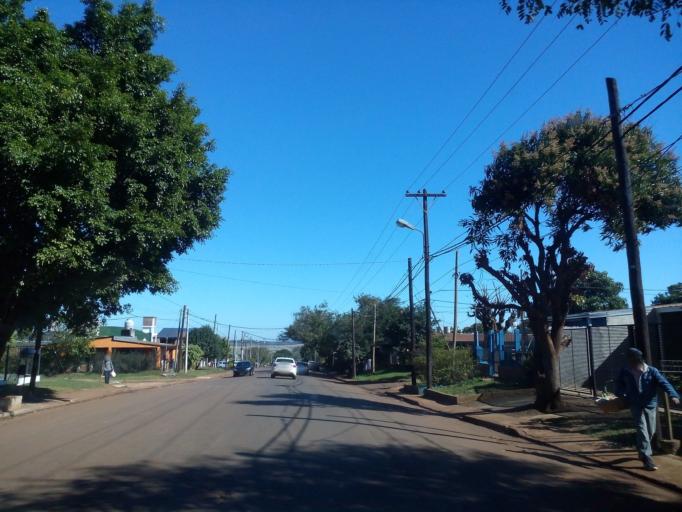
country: AR
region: Misiones
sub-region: Departamento de Capital
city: Posadas
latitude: -27.3871
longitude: -55.9367
